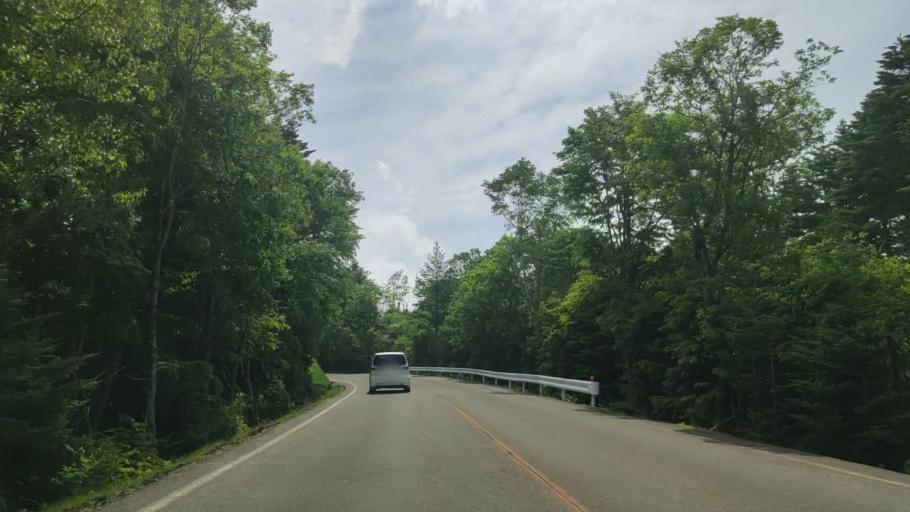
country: JP
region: Yamanashi
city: Fujikawaguchiko
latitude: 35.4095
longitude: 138.6985
